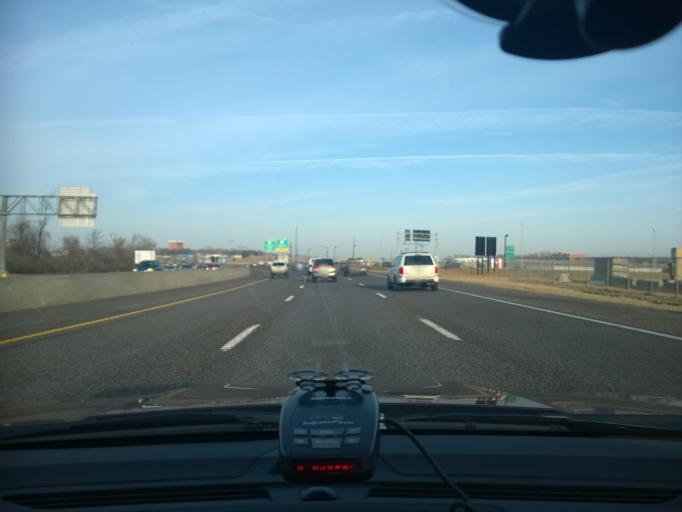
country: US
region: Missouri
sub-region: Saint Louis County
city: Saint Ann
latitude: 38.7425
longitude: -90.3774
